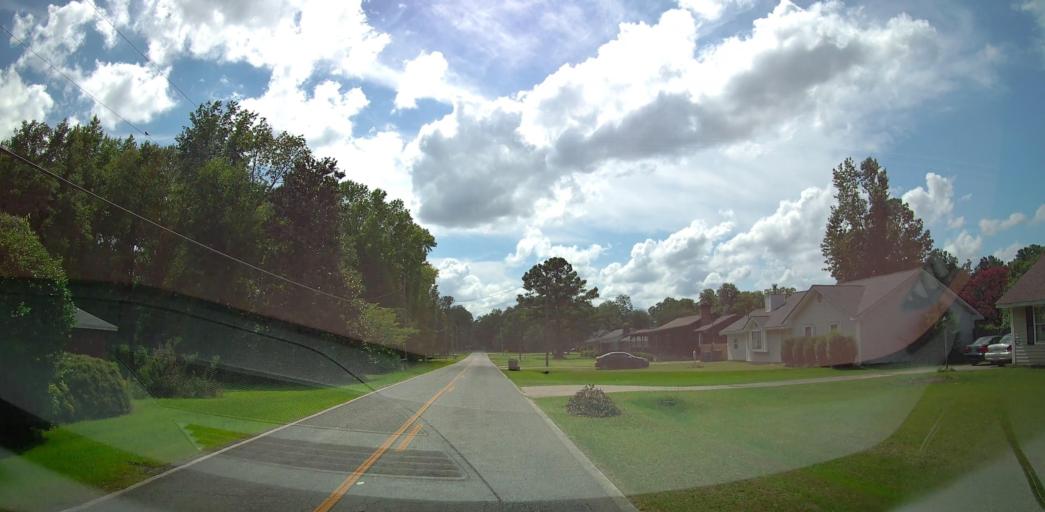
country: US
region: Georgia
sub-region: Houston County
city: Centerville
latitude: 32.7041
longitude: -83.6815
